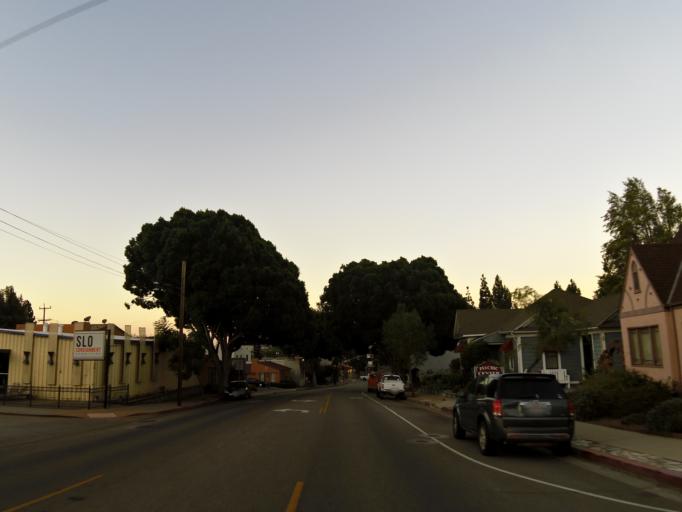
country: US
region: California
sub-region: San Luis Obispo County
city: San Luis Obispo
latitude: 35.2869
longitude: -120.6535
